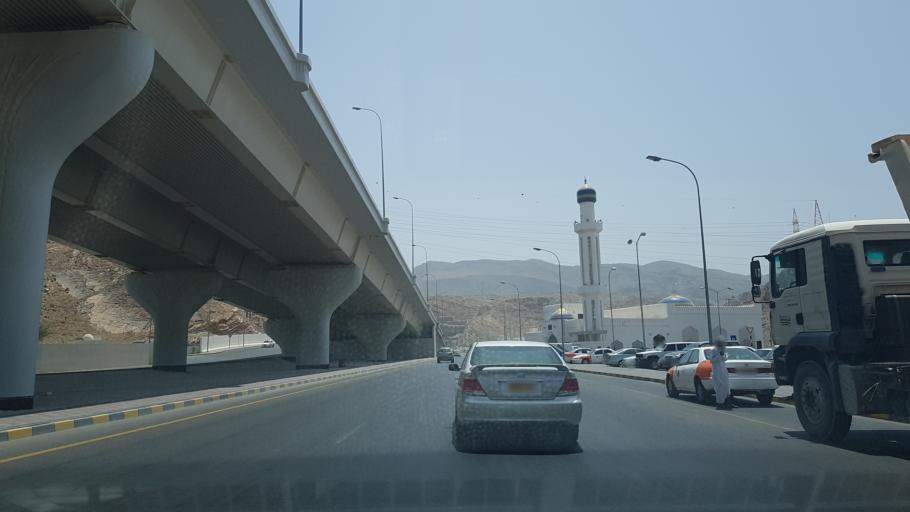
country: OM
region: Muhafazat Masqat
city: Muscat
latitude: 23.5909
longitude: 58.5261
